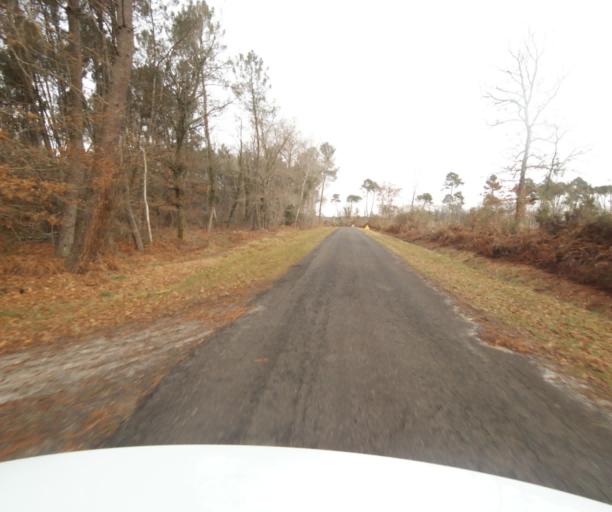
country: FR
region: Aquitaine
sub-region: Departement des Landes
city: Gabarret
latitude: 44.0845
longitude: 0.0716
